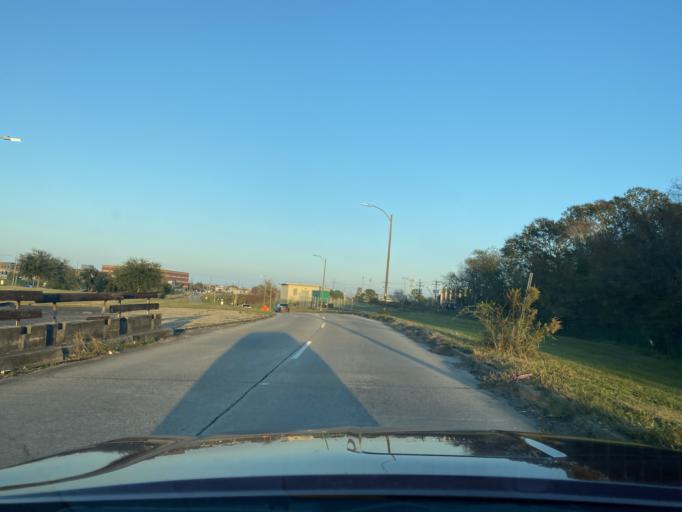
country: US
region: Louisiana
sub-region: Orleans Parish
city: New Orleans
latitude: 30.0272
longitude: -90.0473
